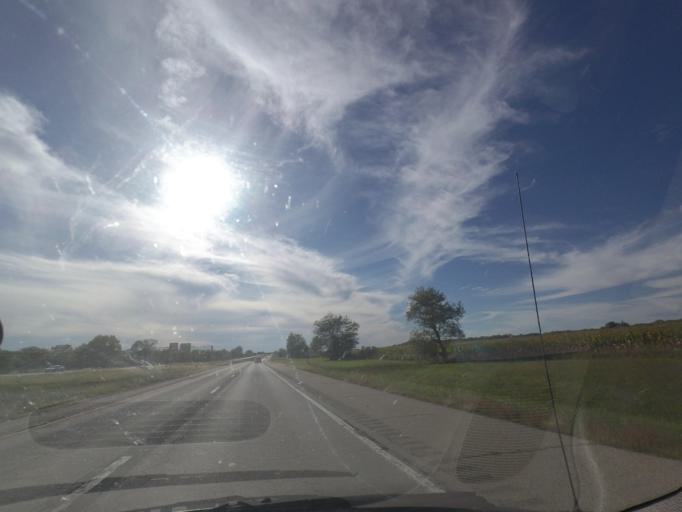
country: US
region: Illinois
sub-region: Macon County
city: Harristown
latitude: 39.8351
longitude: -89.0650
